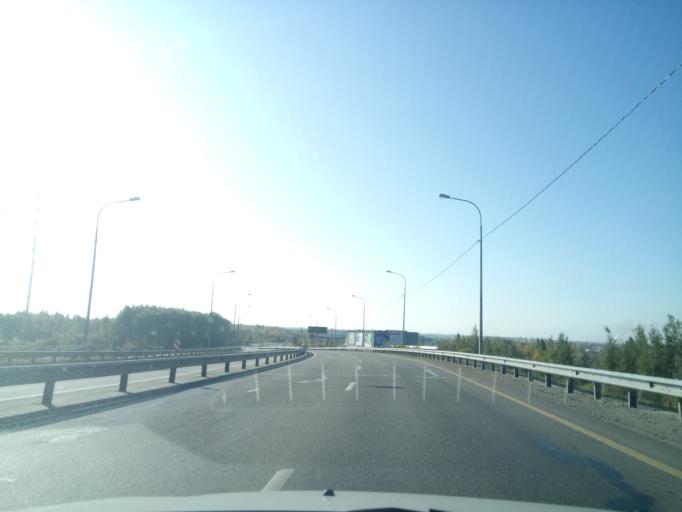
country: RU
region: Nizjnij Novgorod
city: Burevestnik
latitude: 56.1768
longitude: 43.9135
